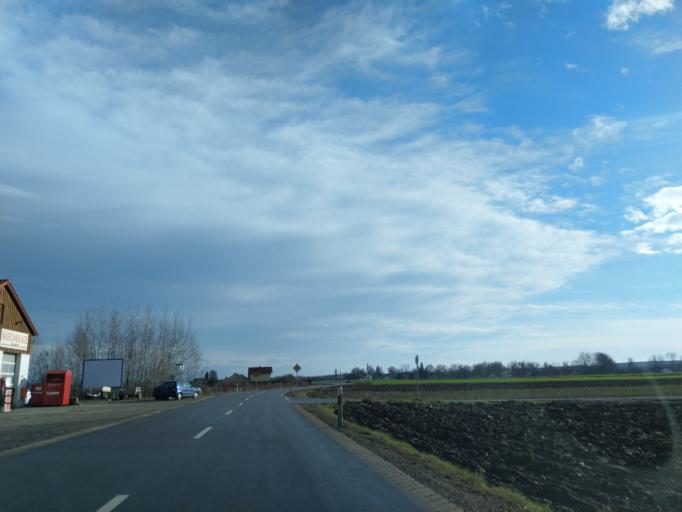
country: DE
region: Bavaria
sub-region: Lower Bavaria
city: Rossbach
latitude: 48.6256
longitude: 12.9627
